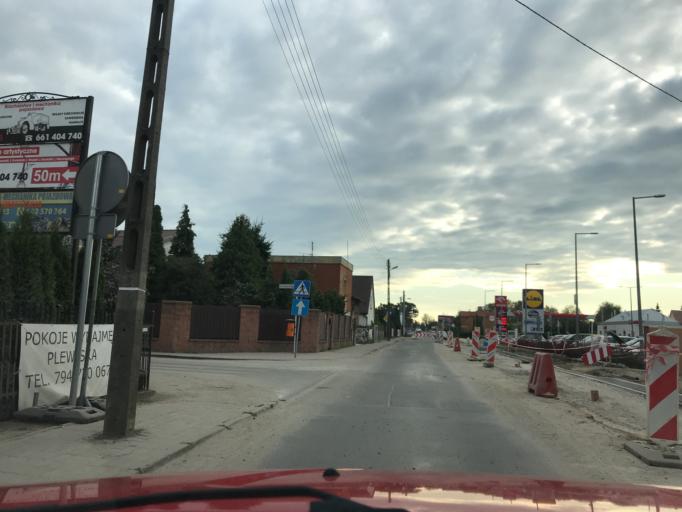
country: PL
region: Greater Poland Voivodeship
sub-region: Powiat poznanski
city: Plewiska
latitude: 52.3675
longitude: 16.8110
